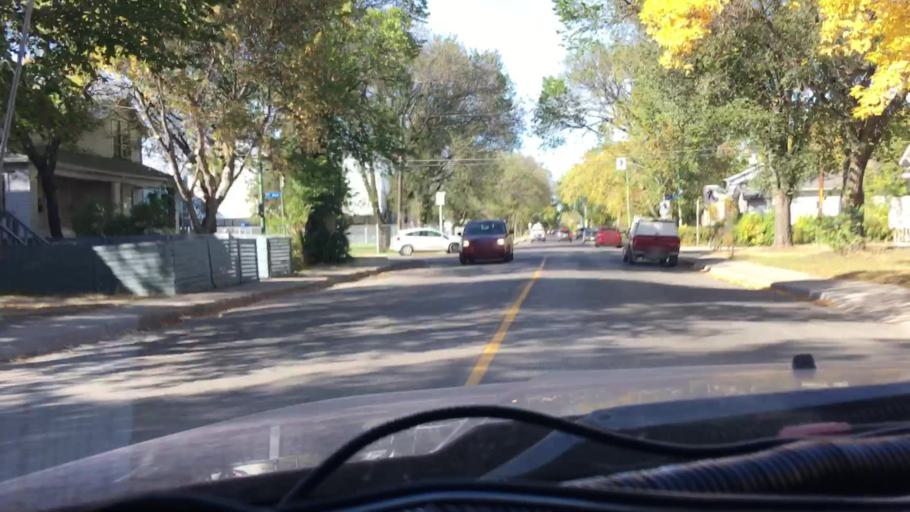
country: CA
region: Saskatchewan
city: Regina
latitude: 50.4563
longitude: -104.6312
